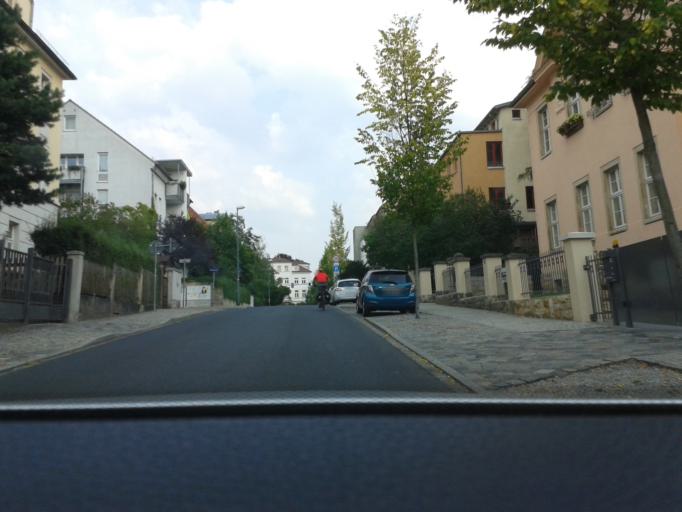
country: DE
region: Saxony
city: Albertstadt
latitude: 51.0678
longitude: 13.7626
